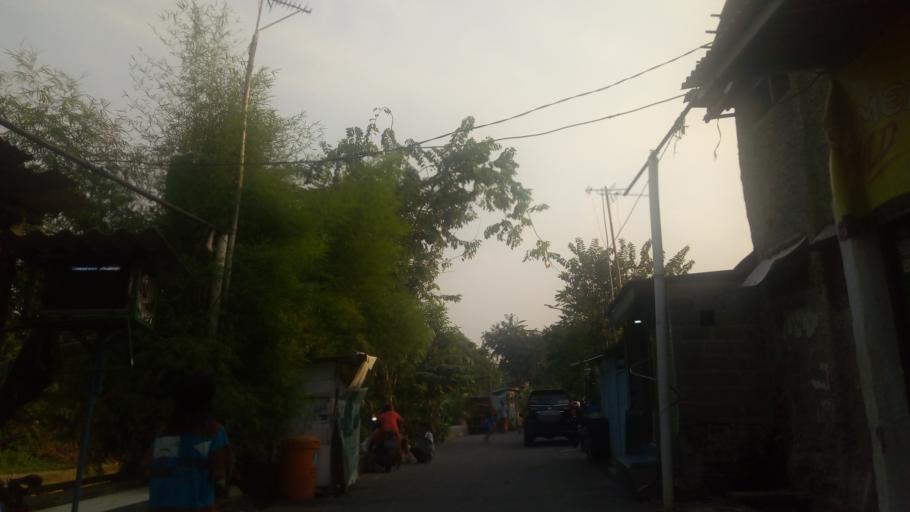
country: ID
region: Jakarta Raya
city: Jakarta
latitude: -6.2052
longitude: 106.8553
